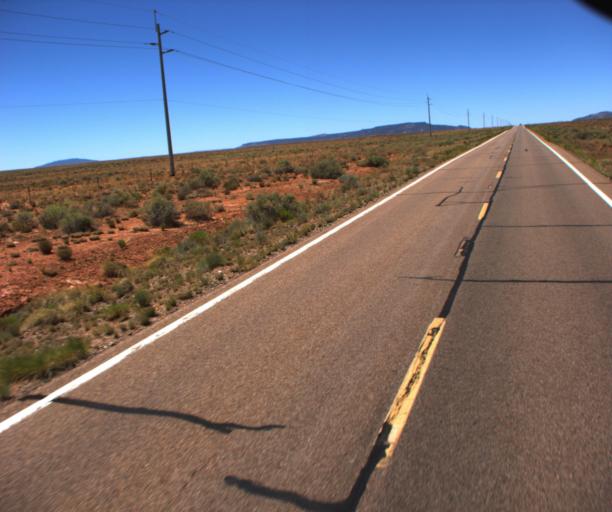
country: US
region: Arizona
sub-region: Coconino County
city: LeChee
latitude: 34.9506
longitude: -110.7621
